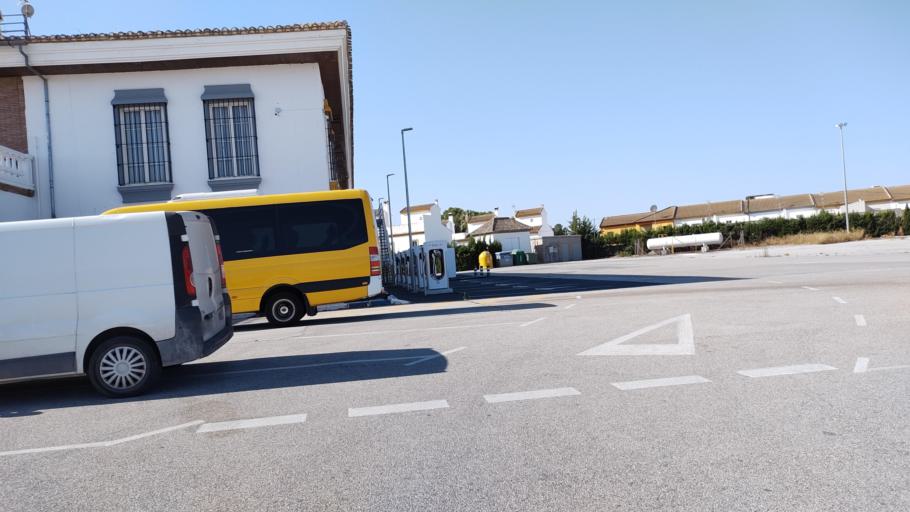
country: ES
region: Andalusia
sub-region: Provincia de Sevilla
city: Aguadulce
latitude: 37.2571
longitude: -4.9860
